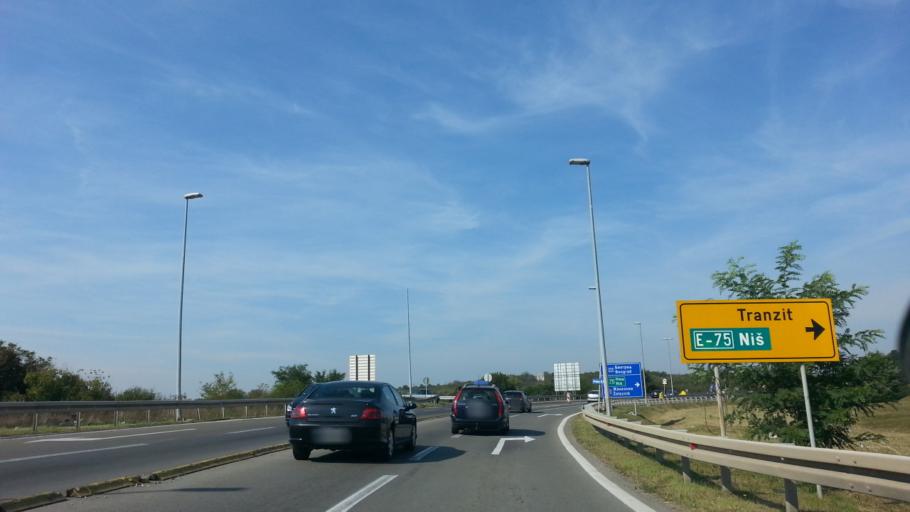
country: RS
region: Central Serbia
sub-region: Belgrade
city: Rakovica
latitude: 44.7166
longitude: 20.4155
